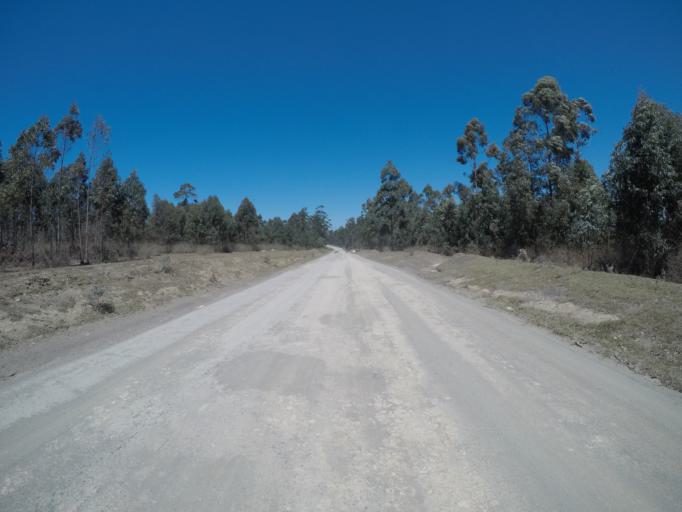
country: ZA
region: Eastern Cape
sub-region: OR Tambo District Municipality
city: Libode
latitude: -31.9535
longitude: 29.0233
